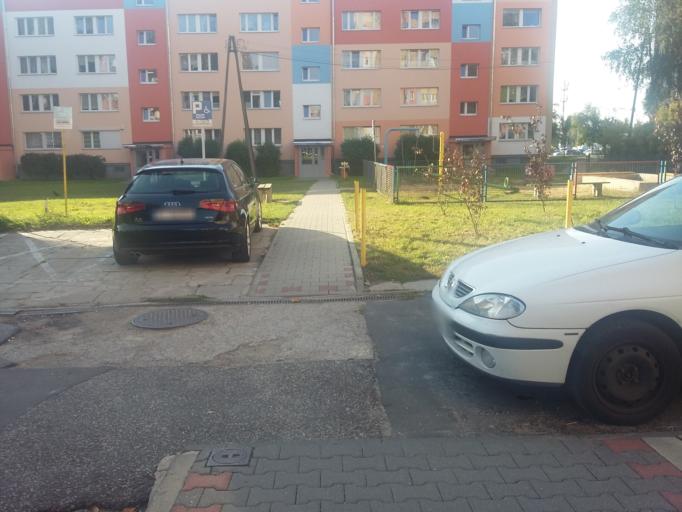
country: PL
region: Lodz Voivodeship
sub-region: Powiat pabianicki
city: Ksawerow
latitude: 51.7426
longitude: 19.4063
